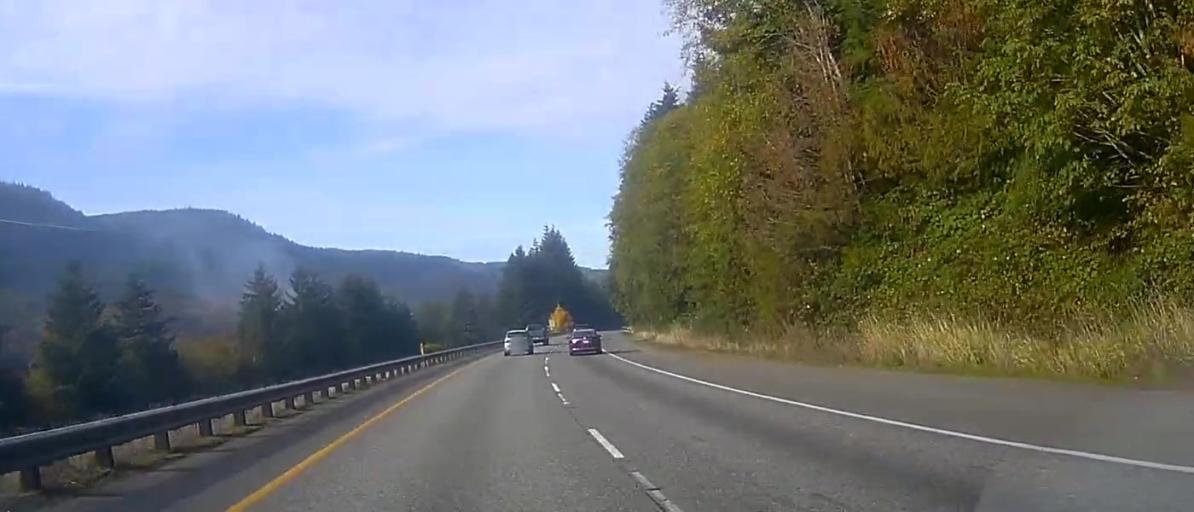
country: US
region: Washington
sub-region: Whatcom County
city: Geneva
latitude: 48.6891
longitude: -122.4212
